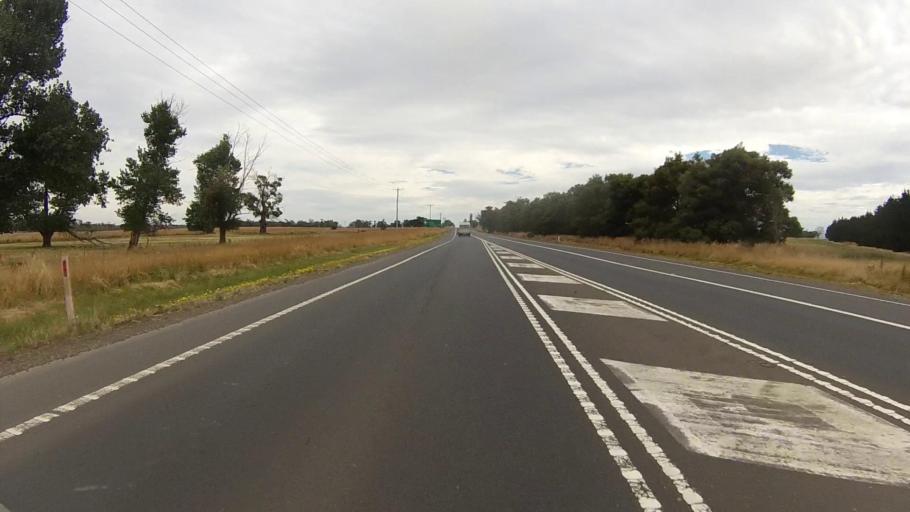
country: AU
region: Tasmania
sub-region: Northern Midlands
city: Evandale
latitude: -41.6850
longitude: 147.2762
